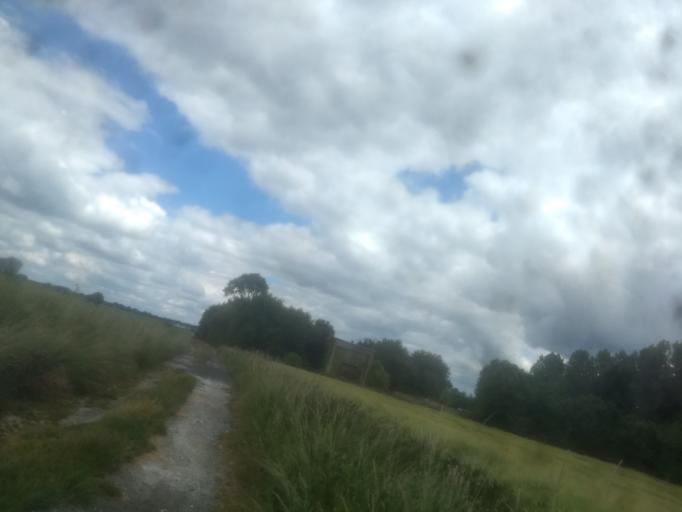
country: FR
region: Nord-Pas-de-Calais
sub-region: Departement du Pas-de-Calais
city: Beaurains
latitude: 50.2133
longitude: 2.7972
